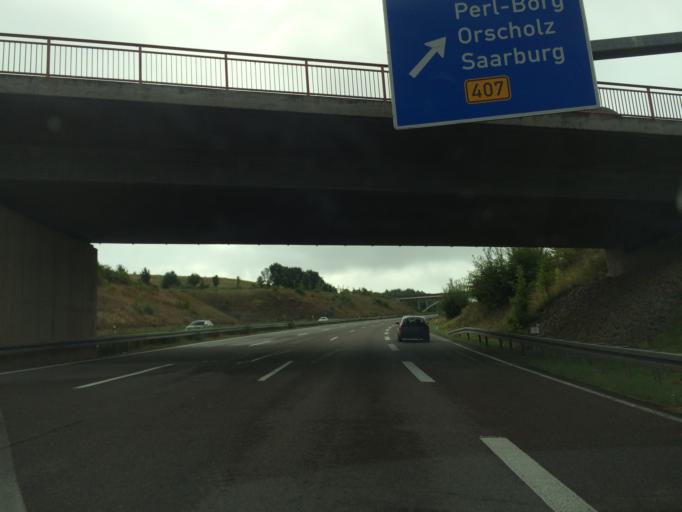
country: DE
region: Saarland
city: Perl
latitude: 49.4874
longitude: 6.4149
